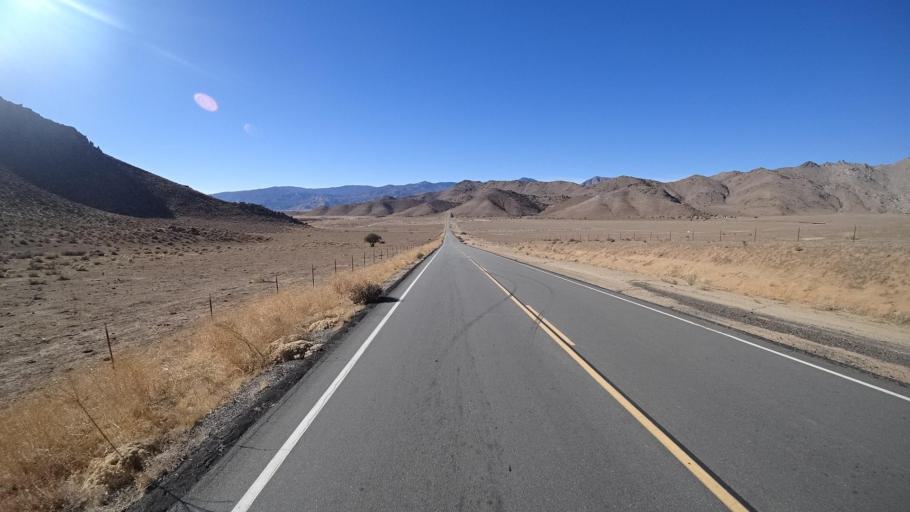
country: US
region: California
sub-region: Kern County
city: Weldon
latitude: 35.6780
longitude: -118.3599
